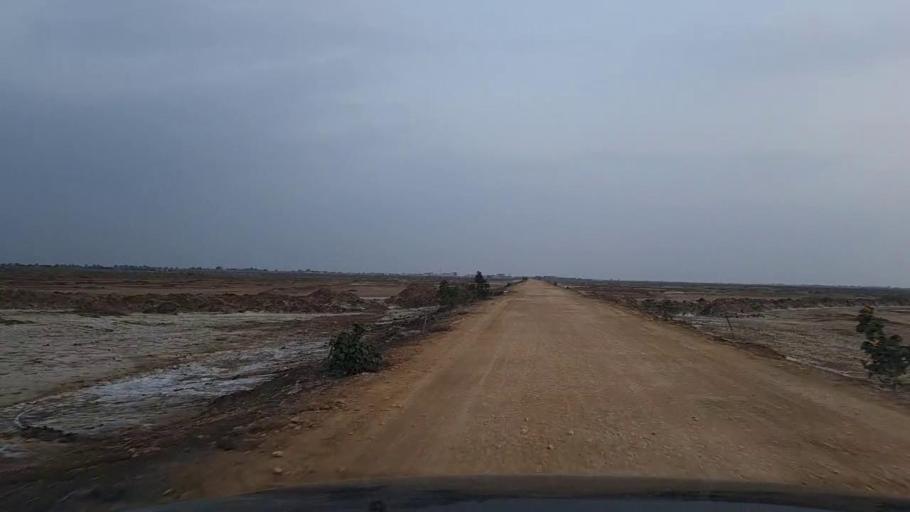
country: PK
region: Sindh
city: Jati
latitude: 24.4992
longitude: 68.3826
